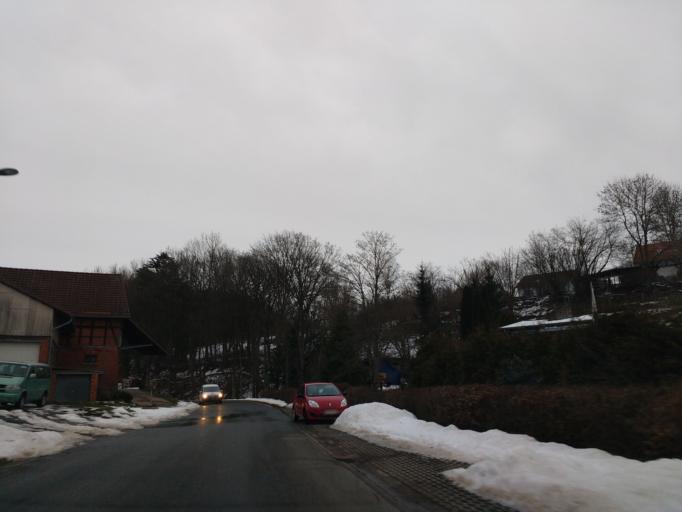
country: DE
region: Thuringia
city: Rohrberg
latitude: 51.4306
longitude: 10.0298
